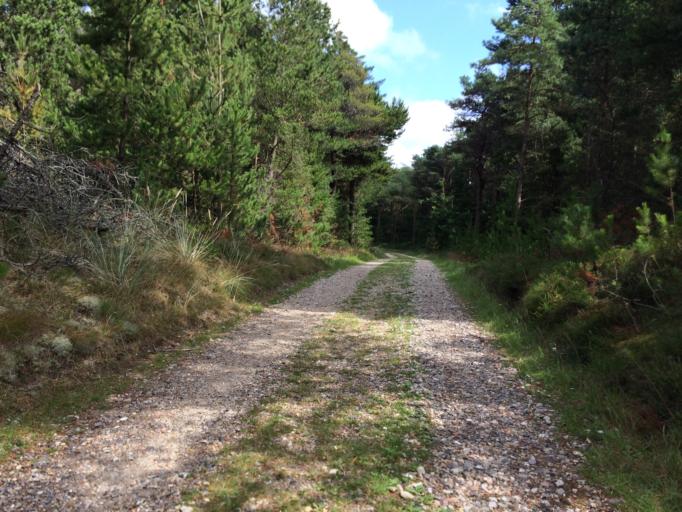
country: DK
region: Central Jutland
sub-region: Holstebro Kommune
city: Ulfborg
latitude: 56.2924
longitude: 8.1512
